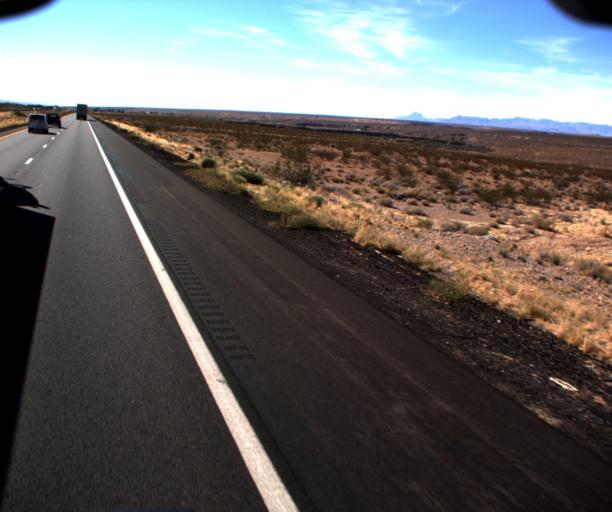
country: US
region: Arizona
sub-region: Mohave County
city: Beaver Dam
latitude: 36.9129
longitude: -113.8821
